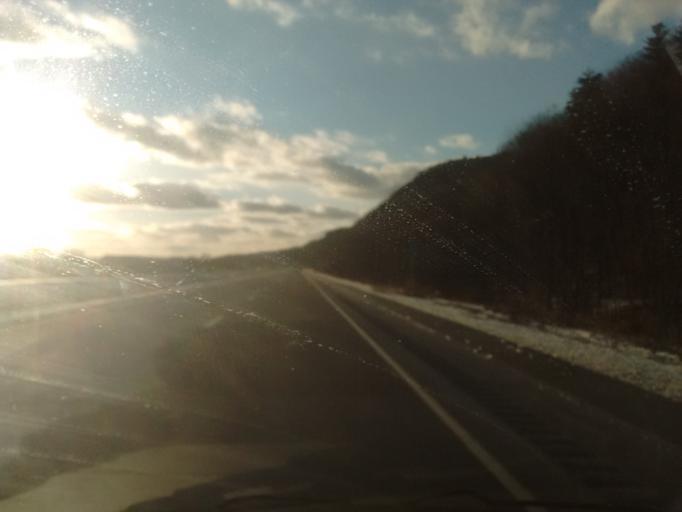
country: US
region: Pennsylvania
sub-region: Pike County
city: Matamoras
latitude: 41.3539
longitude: -74.7291
